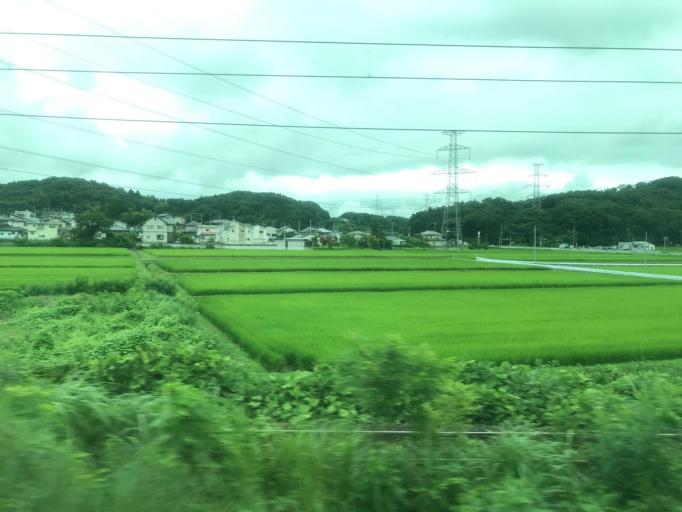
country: JP
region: Fukushima
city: Motomiya
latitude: 37.5415
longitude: 140.4006
